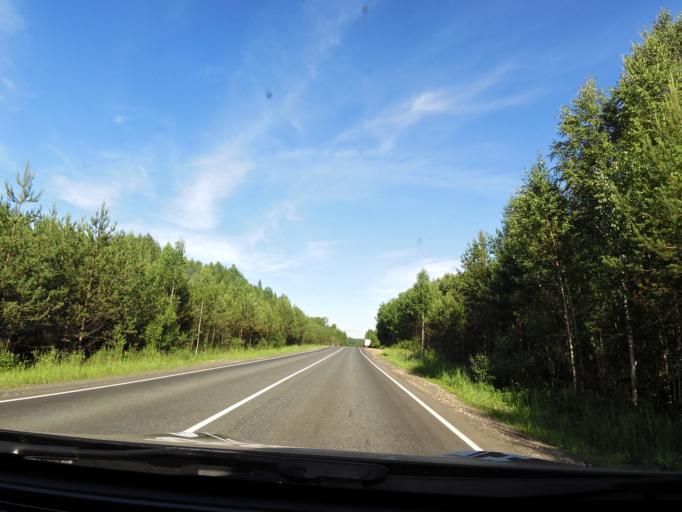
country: RU
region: Kirov
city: Chernaya Kholunitsa
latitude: 58.8735
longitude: 51.5077
